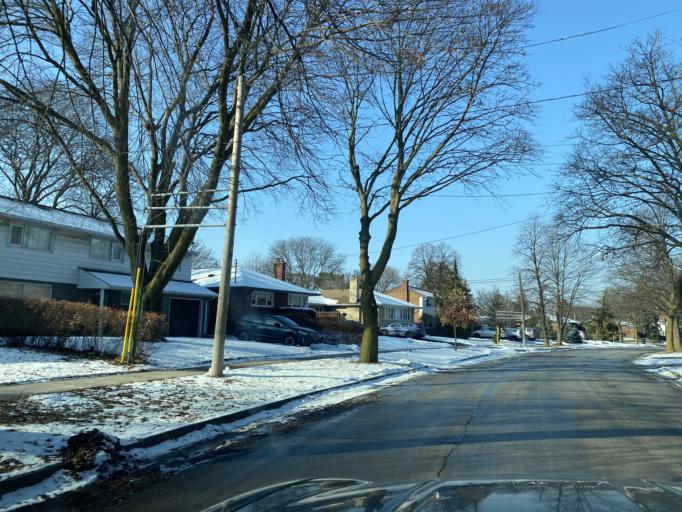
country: CA
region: Ontario
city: Etobicoke
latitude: 43.6610
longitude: -79.5647
